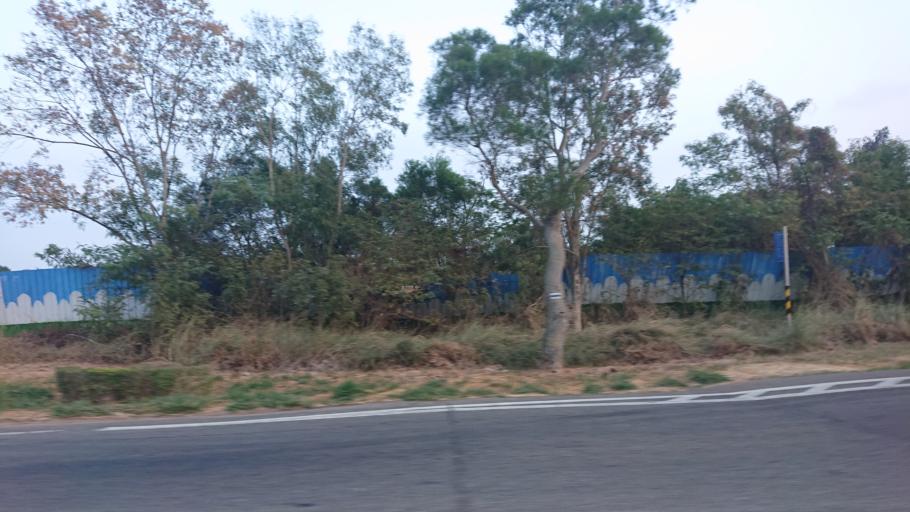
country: TW
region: Fukien
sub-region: Kinmen
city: Jincheng
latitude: 24.4456
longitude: 118.3275
